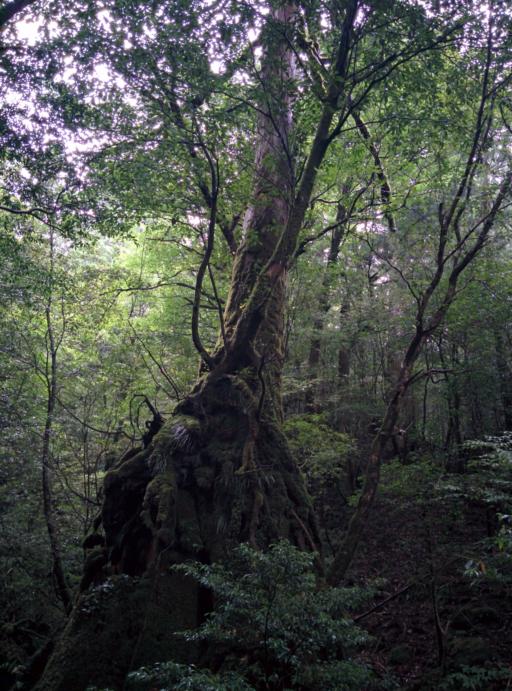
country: JP
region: Kagoshima
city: Nishinoomote
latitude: 30.3662
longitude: 130.5683
